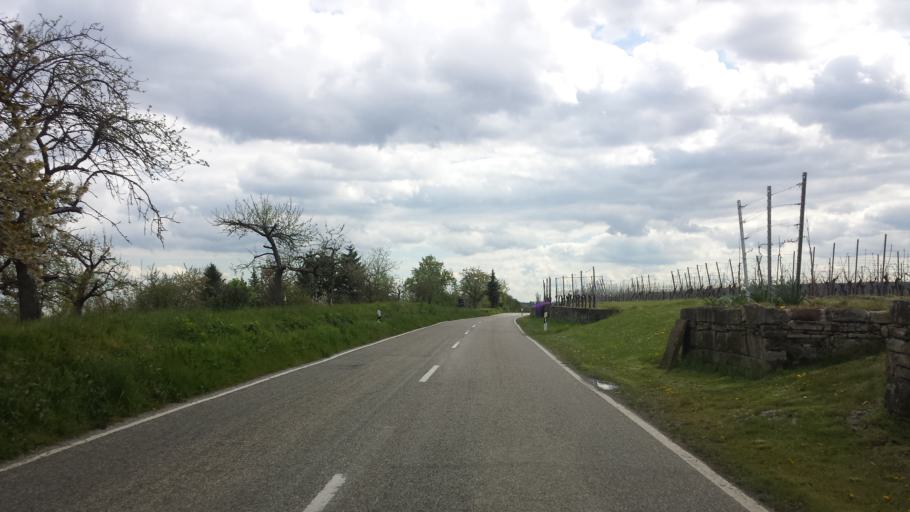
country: DE
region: Baden-Wuerttemberg
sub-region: Regierungsbezirk Stuttgart
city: Vaihingen an der Enz
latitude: 48.9135
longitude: 8.9646
